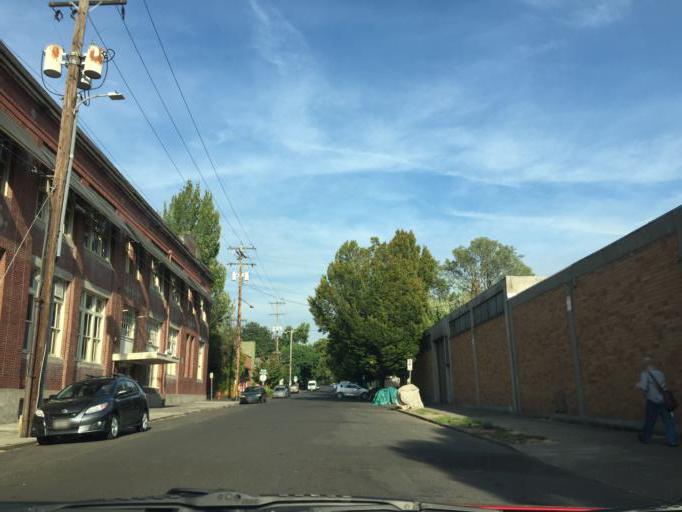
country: US
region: Oregon
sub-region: Multnomah County
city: Portland
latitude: 45.5208
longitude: -122.6555
